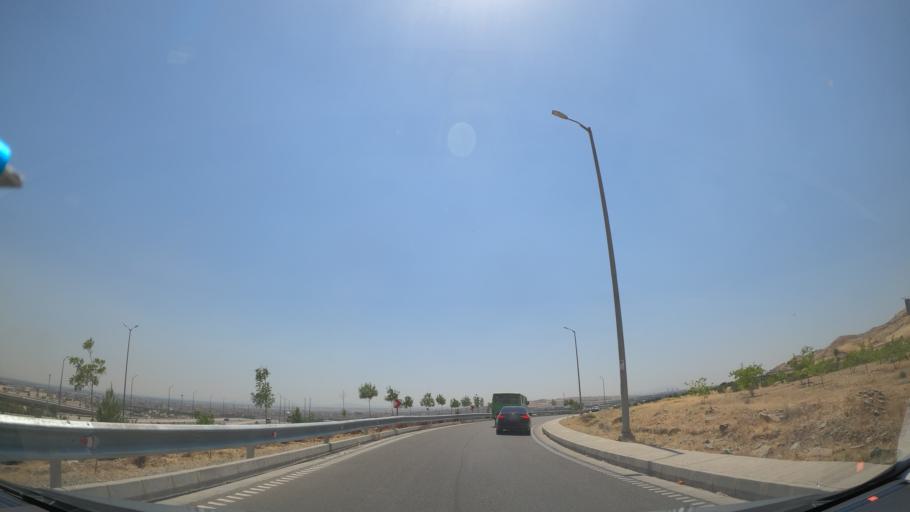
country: IR
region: Tehran
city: Shahr-e Qods
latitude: 35.7449
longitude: 51.1264
